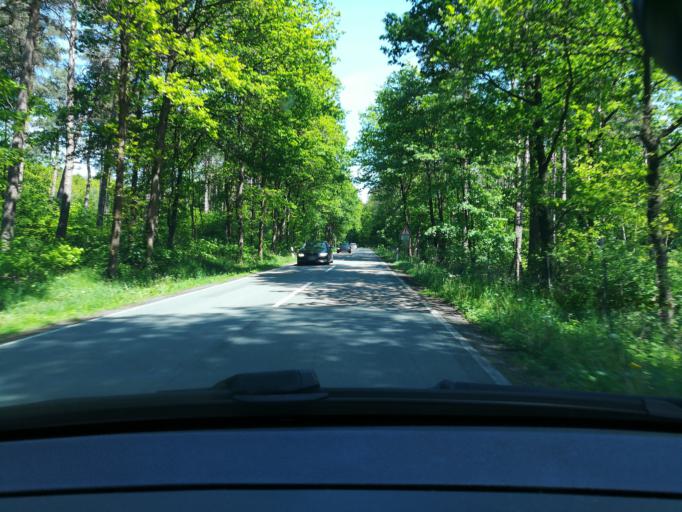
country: DE
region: North Rhine-Westphalia
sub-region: Regierungsbezirk Detmold
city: Oerlinghausen
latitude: 51.9667
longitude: 8.5957
